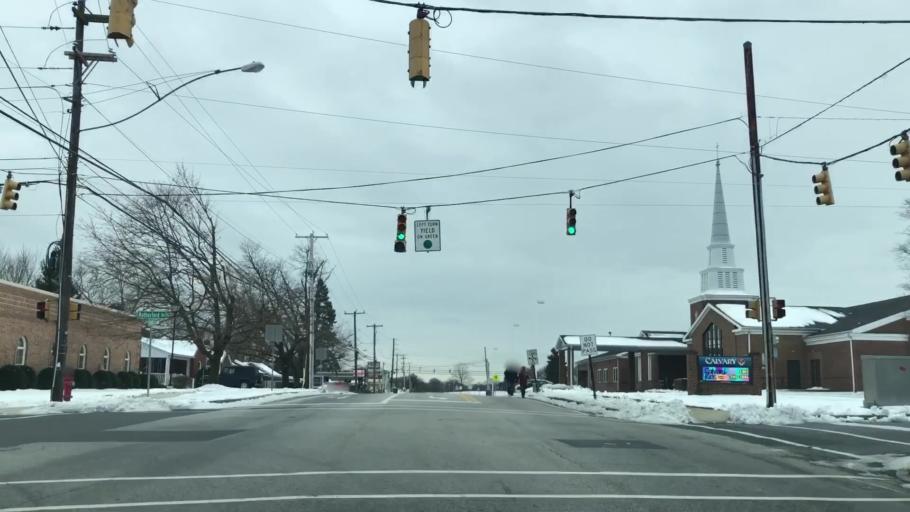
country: US
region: Pennsylvania
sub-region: Dauphin County
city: Colonial Park
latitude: 40.2931
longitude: -76.8072
